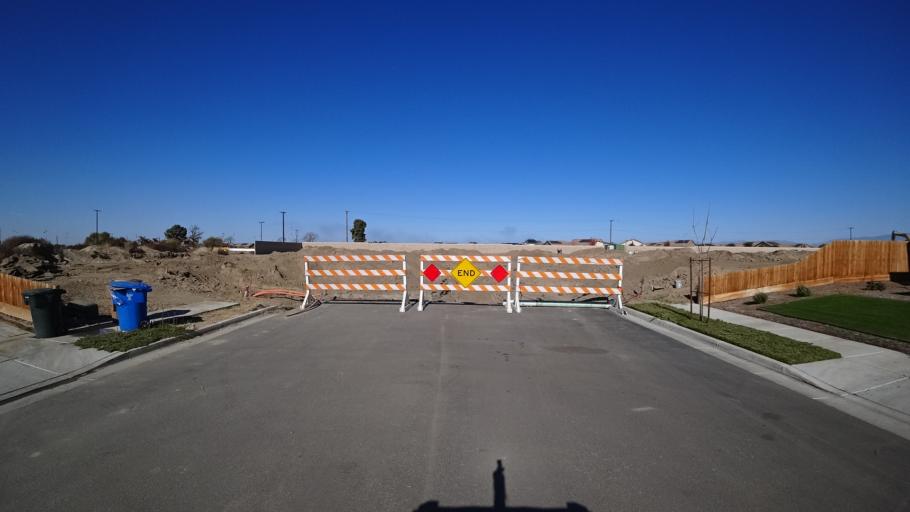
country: US
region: California
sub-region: Kern County
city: Greenfield
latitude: 35.2660
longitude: -119.0717
